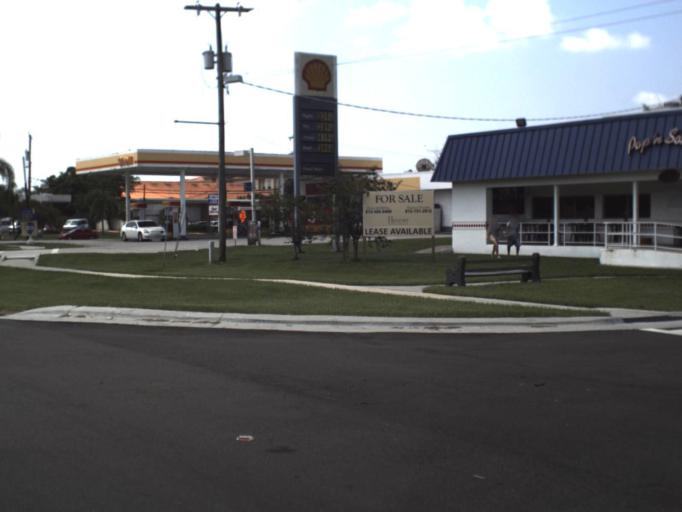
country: US
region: Florida
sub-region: Hillsborough County
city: Egypt Lake-Leto
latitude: 27.9899
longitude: -82.5054
